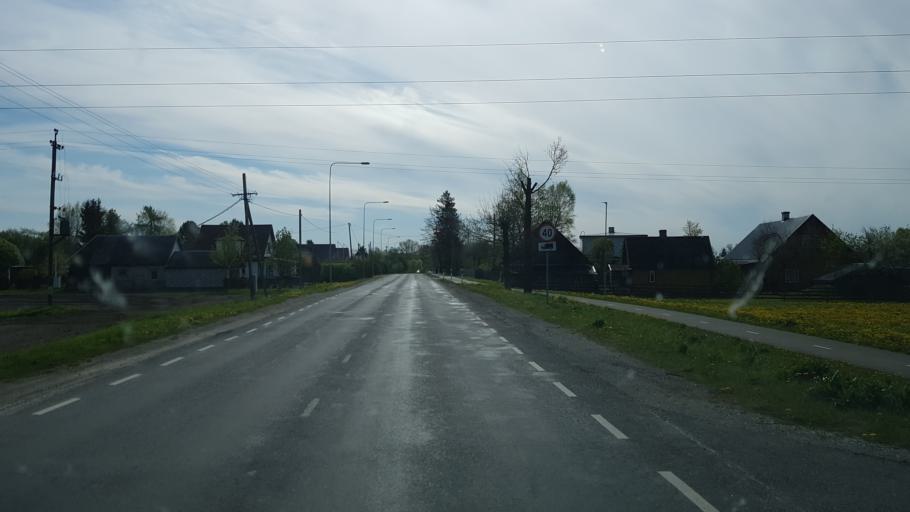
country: EE
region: Ida-Virumaa
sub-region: Kivioli linn
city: Kivioli
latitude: 59.3391
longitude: 27.0023
